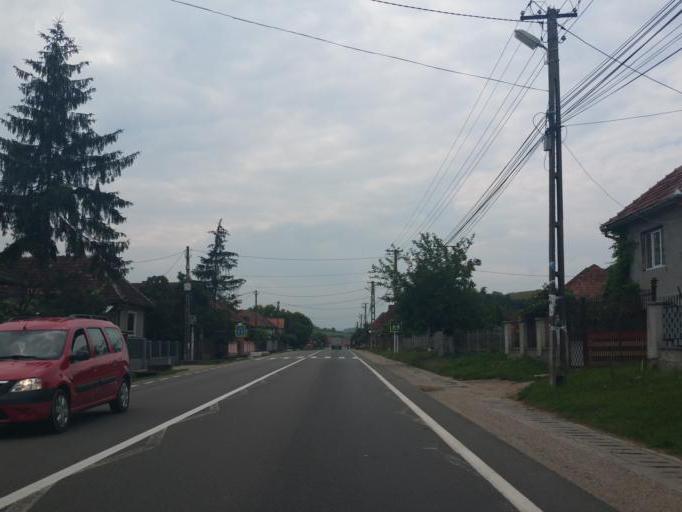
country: RO
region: Salaj
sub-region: Comuna Hida
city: Hida
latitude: 47.0462
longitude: 23.2500
